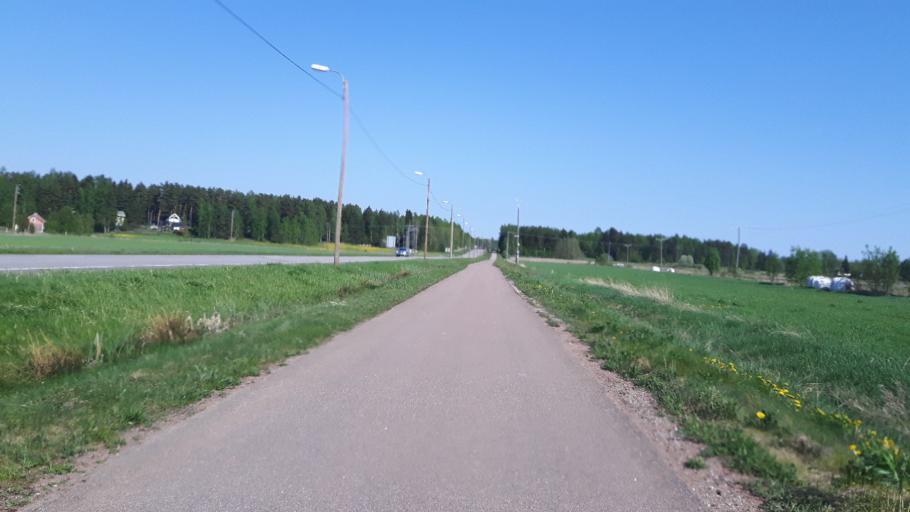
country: FI
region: Kymenlaakso
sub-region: Kotka-Hamina
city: Broby
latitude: 60.4962
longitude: 26.7977
